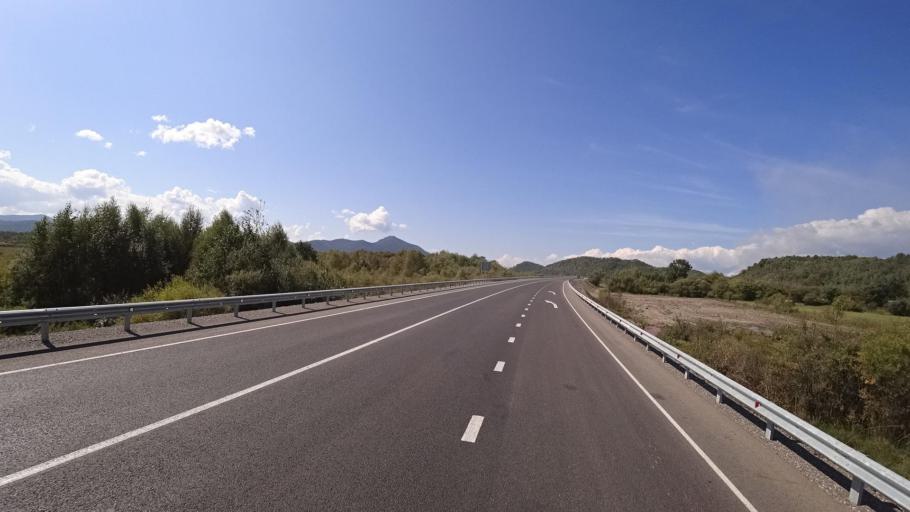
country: RU
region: Jewish Autonomous Oblast
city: Londoko
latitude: 49.0015
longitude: 131.9426
